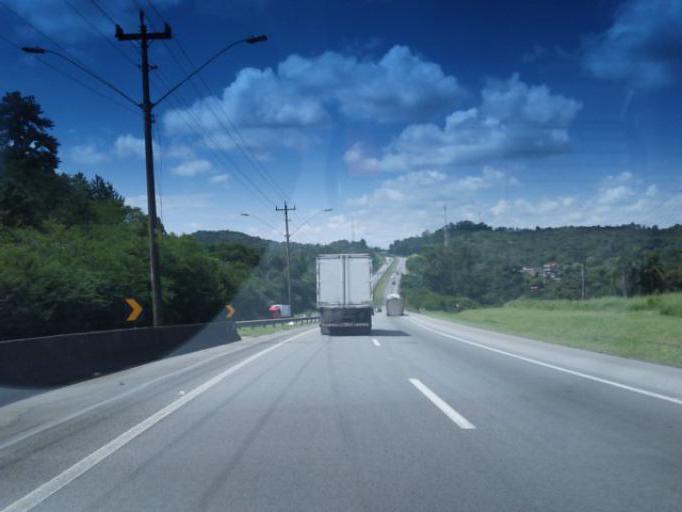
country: BR
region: Sao Paulo
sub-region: Sao Lourenco Da Serra
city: Sao Lourenco da Serra
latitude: -23.8127
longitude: -46.9232
